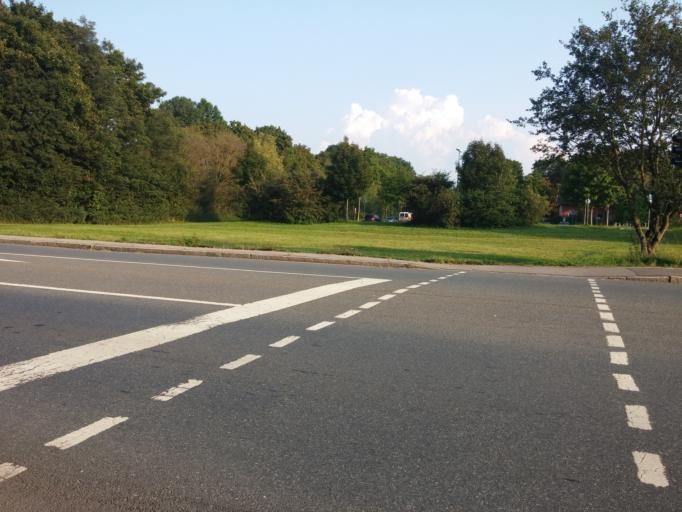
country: DE
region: Bavaria
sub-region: Upper Bavaria
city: Kirchheim bei Muenchen
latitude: 48.1662
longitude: 11.7817
